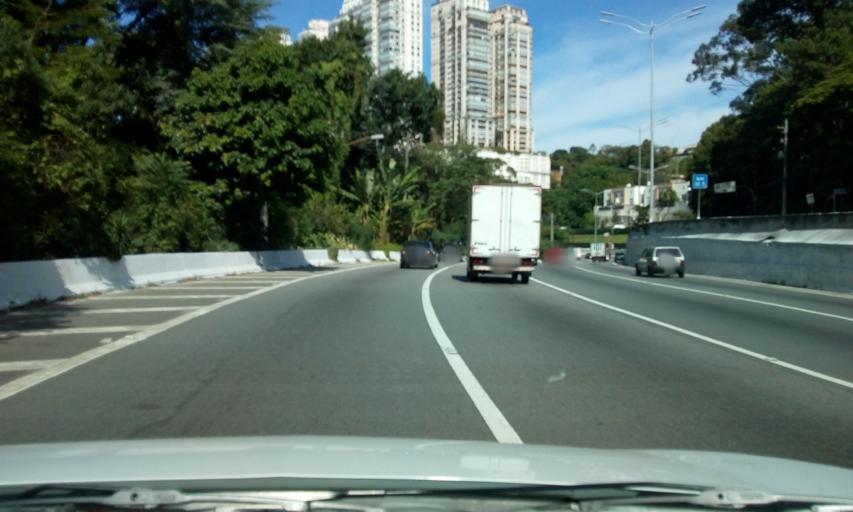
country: BR
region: Sao Paulo
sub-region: Sao Paulo
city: Sao Paulo
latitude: -23.5953
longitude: -46.6953
